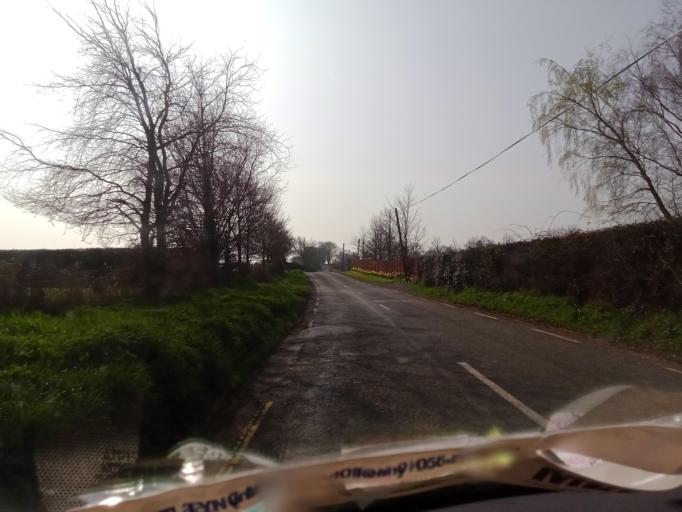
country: IE
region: Leinster
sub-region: Kilkenny
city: Callan
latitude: 52.5065
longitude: -7.3836
